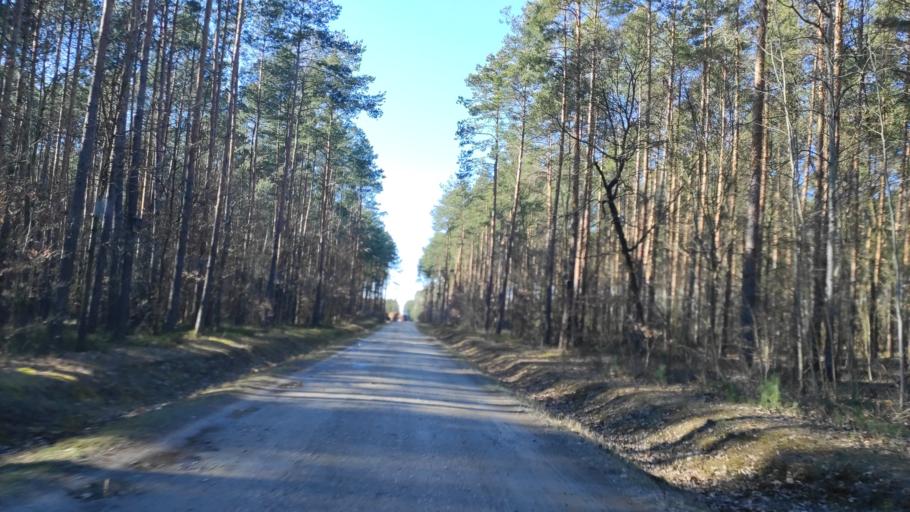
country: PL
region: Masovian Voivodeship
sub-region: Powiat radomski
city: Jedlnia-Letnisko
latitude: 51.4625
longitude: 21.3235
